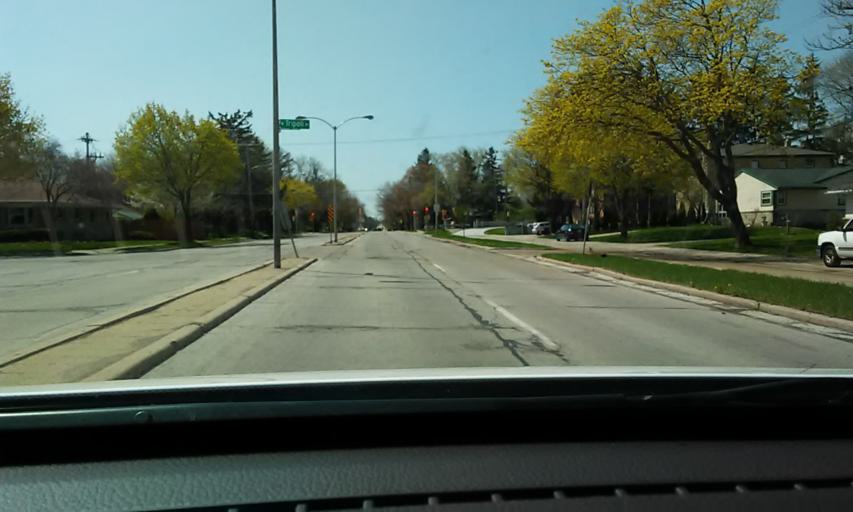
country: US
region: Wisconsin
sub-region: Milwaukee County
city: Greenfield
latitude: 42.9750
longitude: -87.9980
